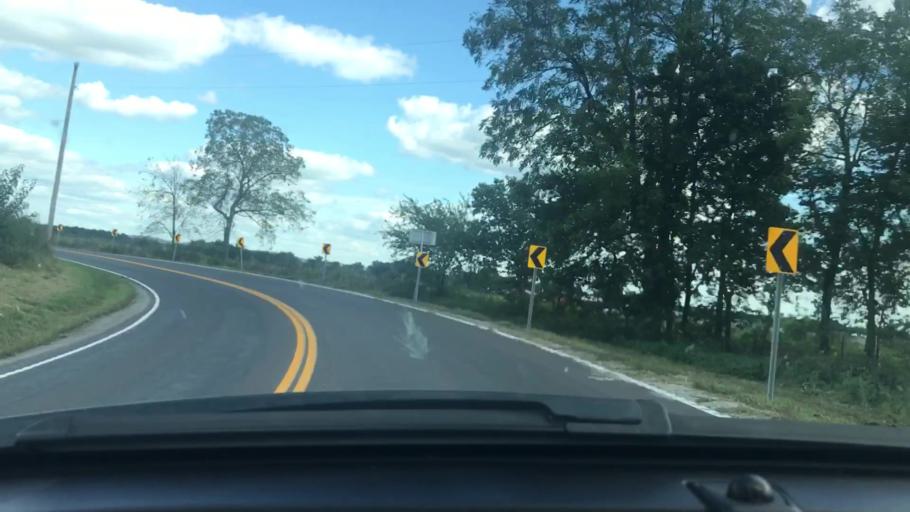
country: US
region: Missouri
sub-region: Wright County
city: Mountain Grove
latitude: 37.1656
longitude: -92.2669
